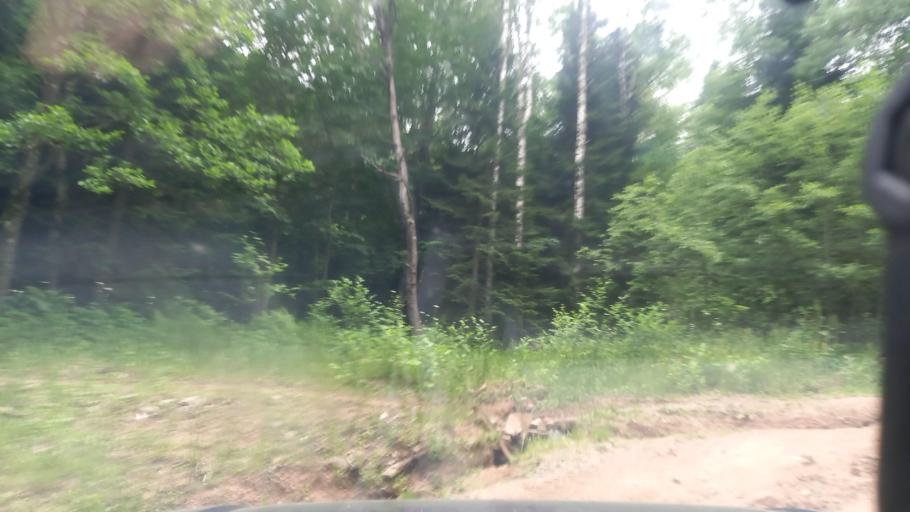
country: RU
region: Karachayevo-Cherkesiya
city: Kurdzhinovo
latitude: 43.8098
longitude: 40.8669
